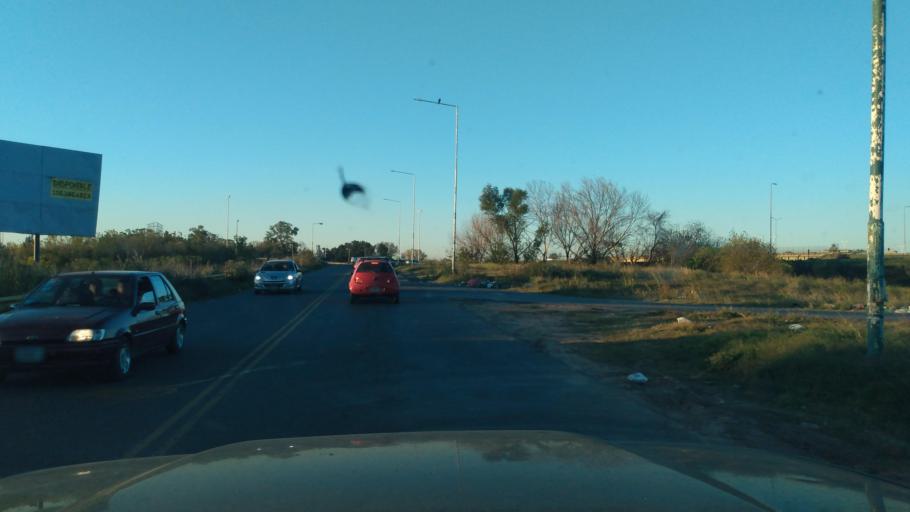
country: AR
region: Buenos Aires
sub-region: Partido de Merlo
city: Merlo
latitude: -34.6299
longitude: -58.7244
